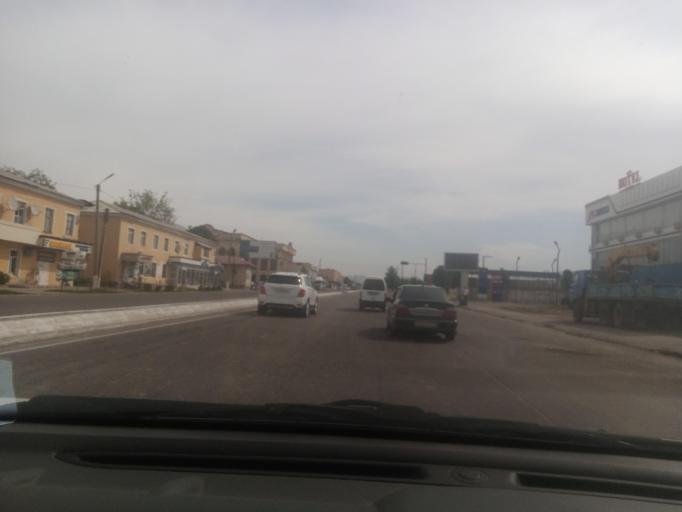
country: UZ
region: Toshkent
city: Angren
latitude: 41.0076
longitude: 70.0922
